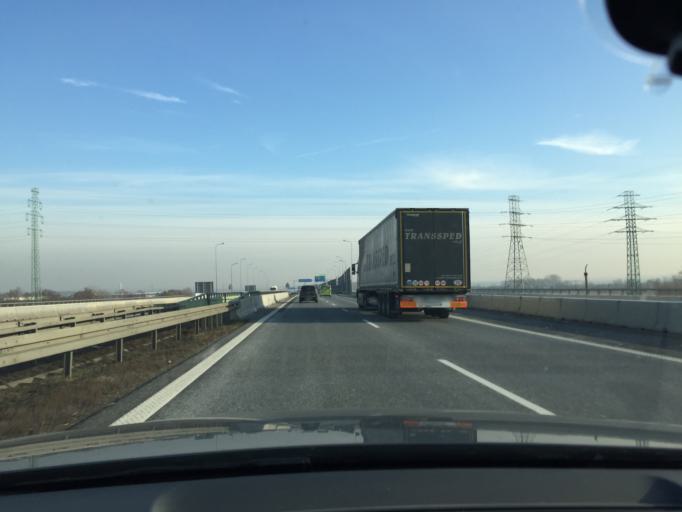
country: PL
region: Silesian Voivodeship
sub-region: Gliwice
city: Gliwice
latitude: 50.2589
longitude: 18.6988
